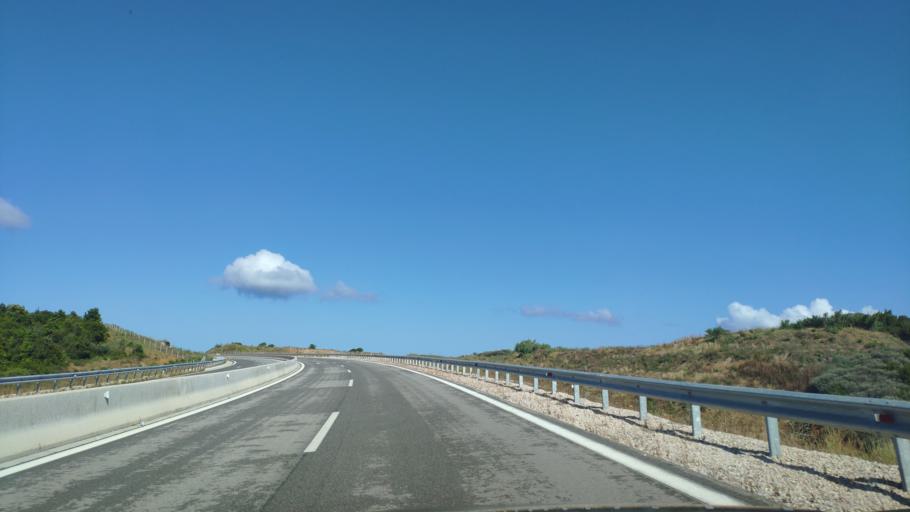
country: GR
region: West Greece
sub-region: Nomos Aitolias kai Akarnanias
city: Vonitsa
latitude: 38.9152
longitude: 20.8241
